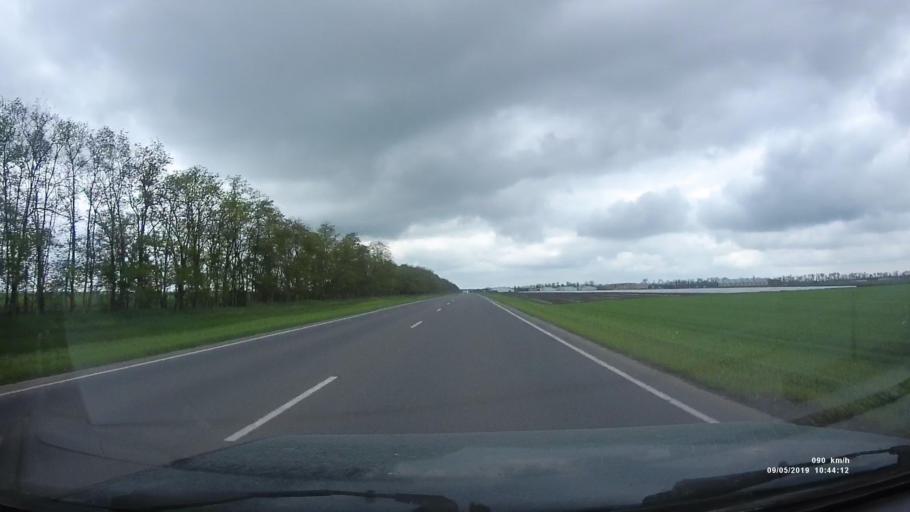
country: RU
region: Rostov
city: Peshkovo
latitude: 47.0030
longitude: 39.3917
